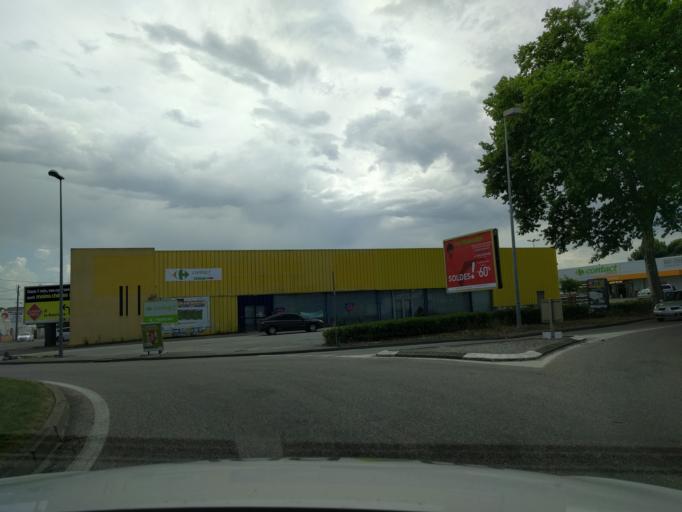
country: FR
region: Languedoc-Roussillon
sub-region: Departement de l'Aude
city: Carcassonne
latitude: 43.2114
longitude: 2.3241
